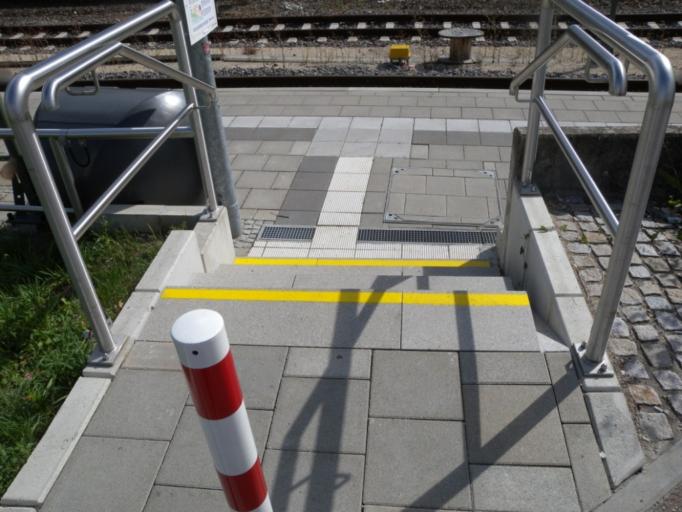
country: DE
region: Baden-Wuerttemberg
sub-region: Regierungsbezirk Stuttgart
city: Kirchheim unter Teck
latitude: 48.6440
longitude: 9.4454
